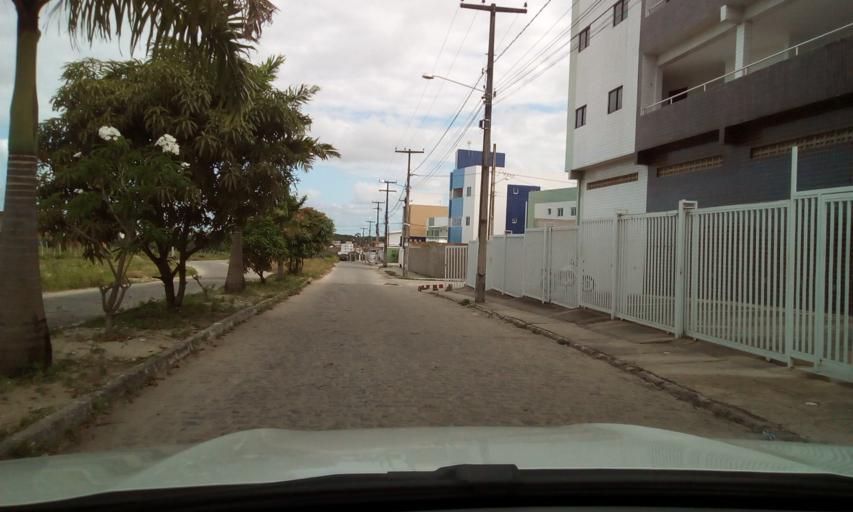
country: BR
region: Paraiba
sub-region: Joao Pessoa
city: Joao Pessoa
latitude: -7.1856
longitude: -34.8794
